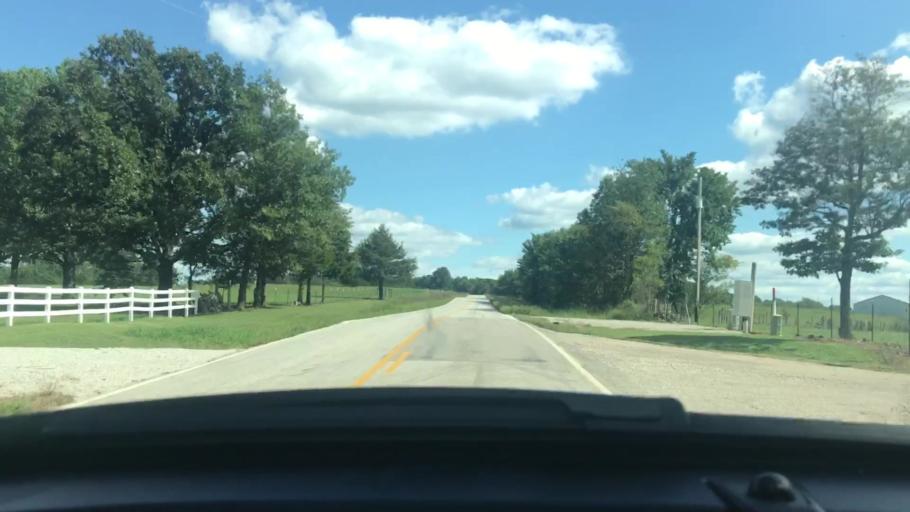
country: US
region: Missouri
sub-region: Wright County
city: Hartville
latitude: 37.3813
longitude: -92.4379
